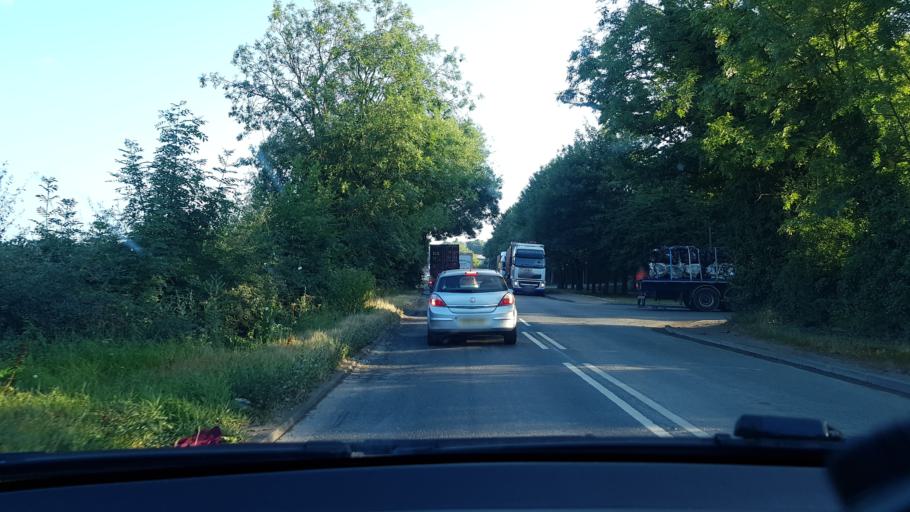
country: GB
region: England
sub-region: Derbyshire
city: Ilkeston
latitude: 52.9526
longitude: -1.3070
